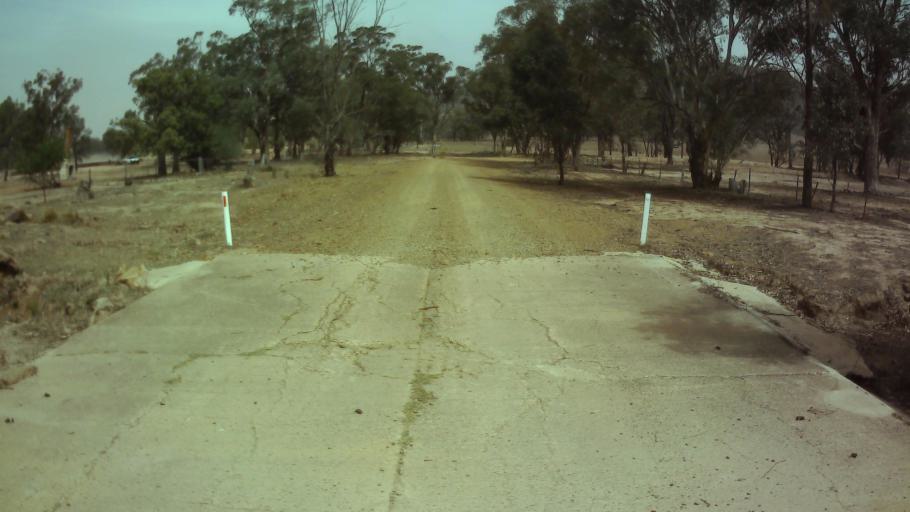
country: AU
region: New South Wales
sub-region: Weddin
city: Grenfell
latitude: -33.7435
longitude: 147.9617
